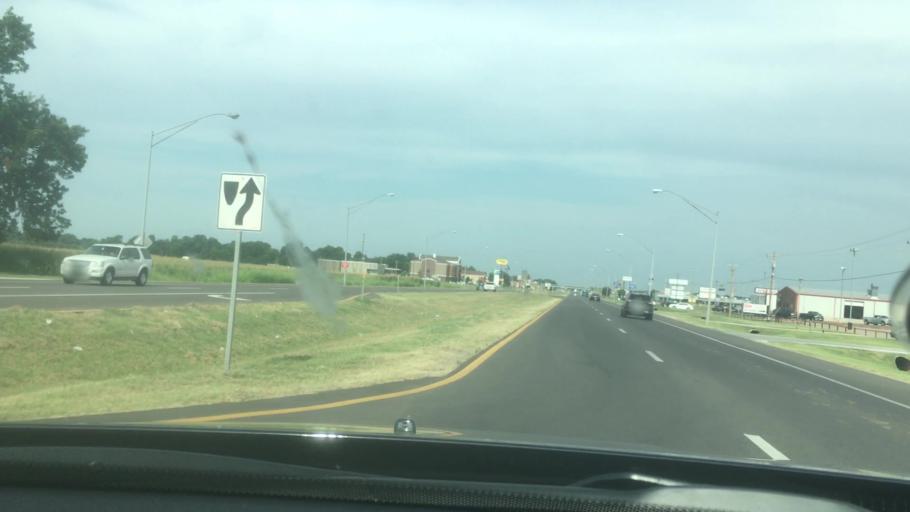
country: US
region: Oklahoma
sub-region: Garvin County
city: Pauls Valley
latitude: 34.7393
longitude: -97.2498
